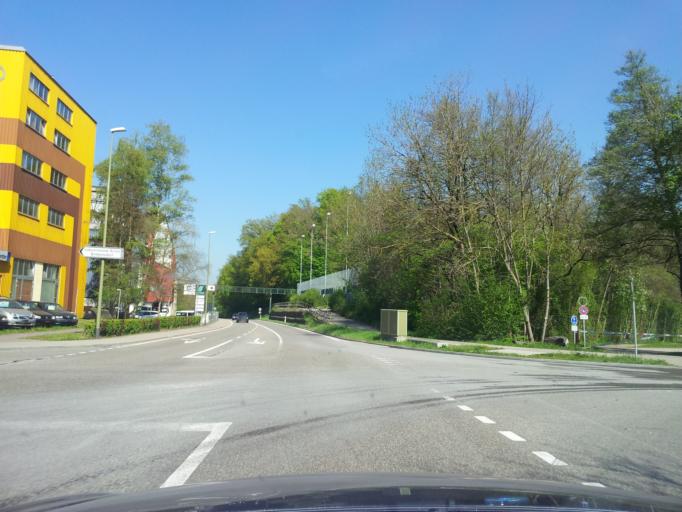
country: CH
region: Zurich
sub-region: Bezirk Dietikon
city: Urdorf / Oberurdorf
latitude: 47.3658
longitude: 8.4301
